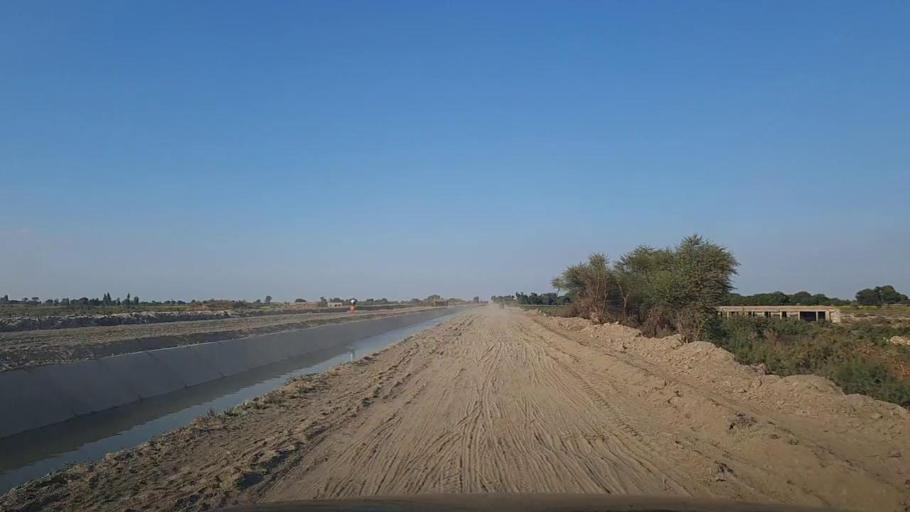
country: PK
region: Sindh
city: Jhol
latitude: 25.8907
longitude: 69.0381
